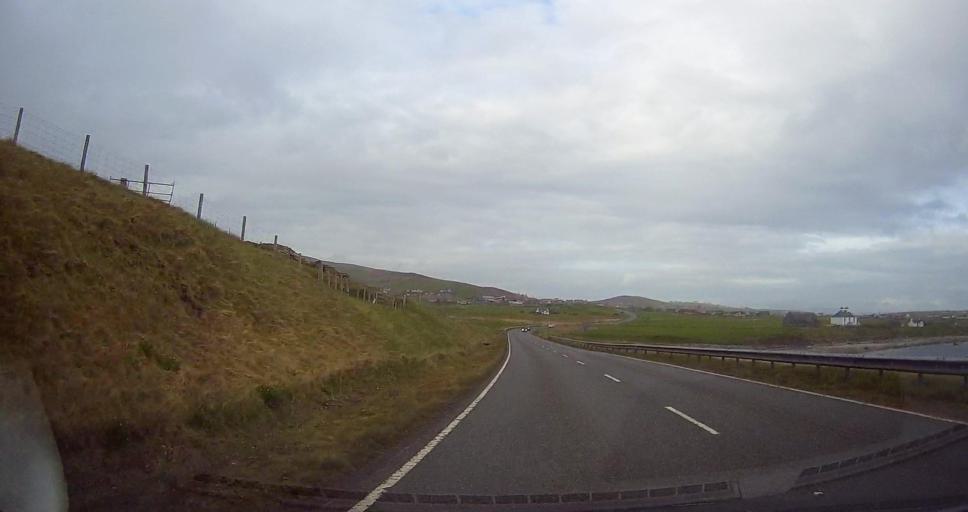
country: GB
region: Scotland
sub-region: Shetland Islands
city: Sandwick
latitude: 60.0318
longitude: -1.2337
